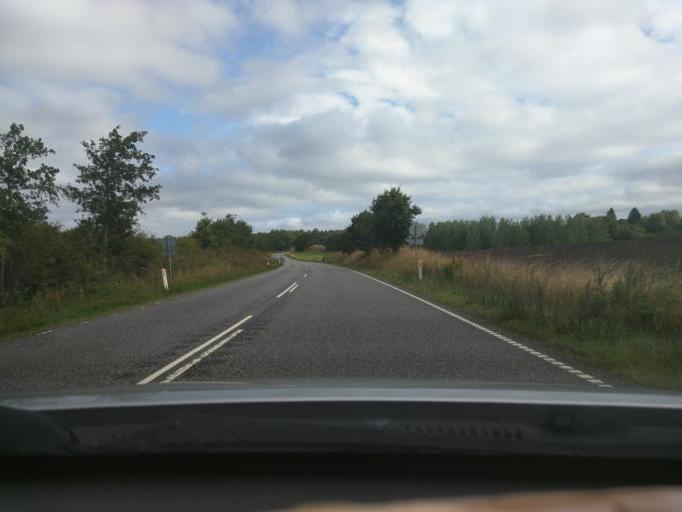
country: DK
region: Central Jutland
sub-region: Viborg Kommune
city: Viborg
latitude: 56.3599
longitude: 9.3670
